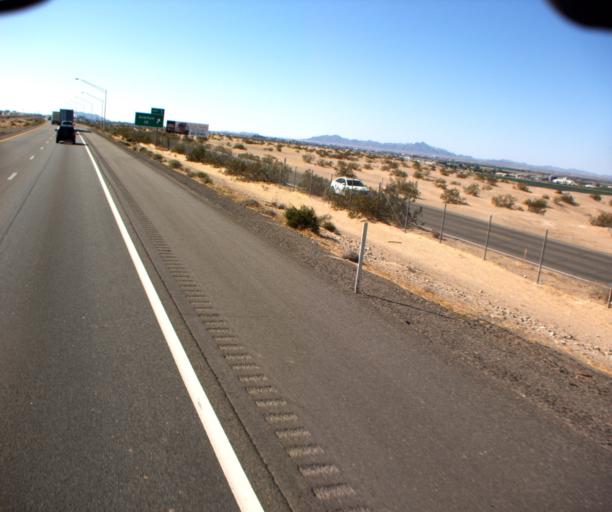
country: US
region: Arizona
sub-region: Yuma County
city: Yuma
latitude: 32.6870
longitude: -114.5705
